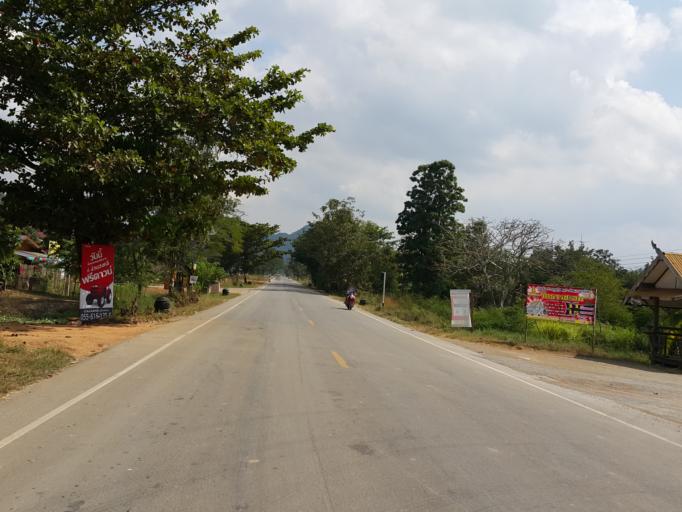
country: TH
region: Sukhothai
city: Thung Saliam
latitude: 17.3353
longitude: 99.4829
